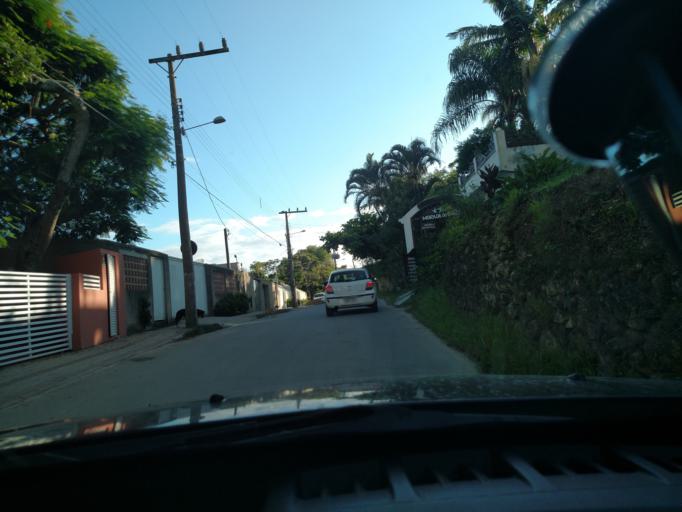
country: BR
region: Santa Catarina
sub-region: Porto Belo
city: Porto Belo
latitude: -27.1446
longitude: -48.4790
